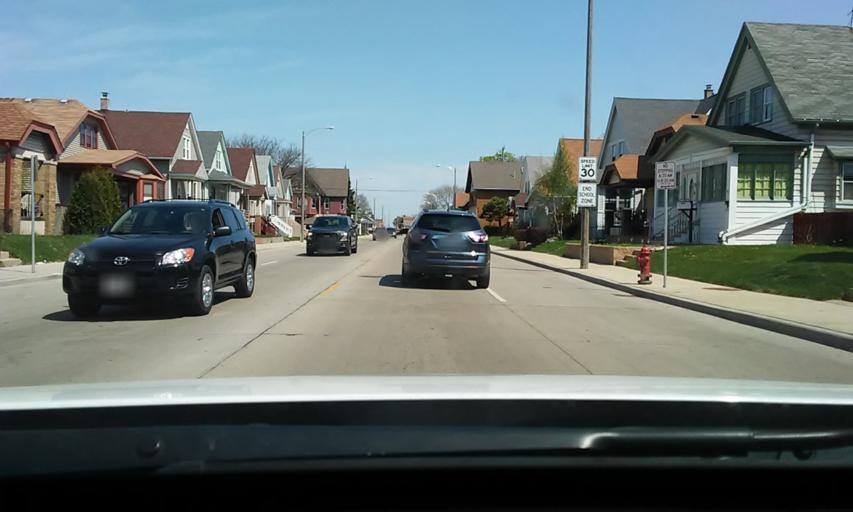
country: US
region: Wisconsin
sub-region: Milwaukee County
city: West Milwaukee
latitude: 43.0131
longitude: -87.9575
